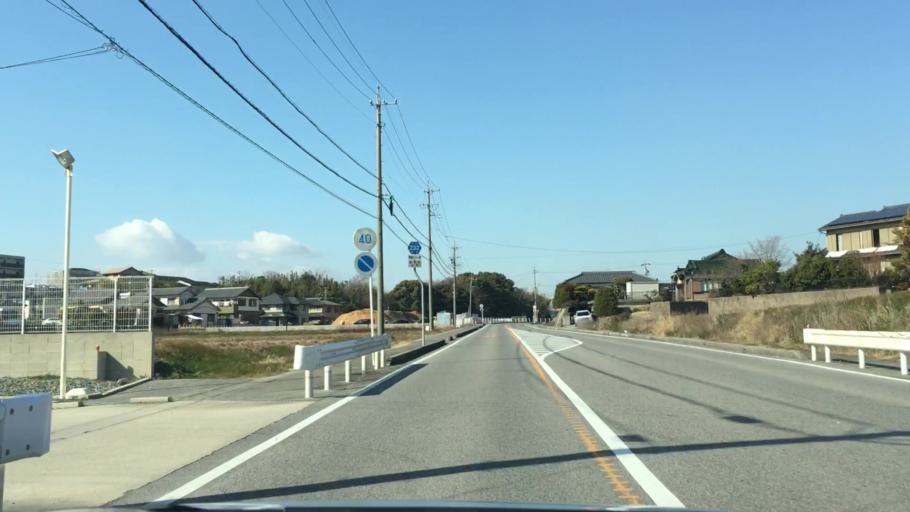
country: JP
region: Aichi
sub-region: Toyota-shi
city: Toyota
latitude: 35.0466
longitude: 137.1141
